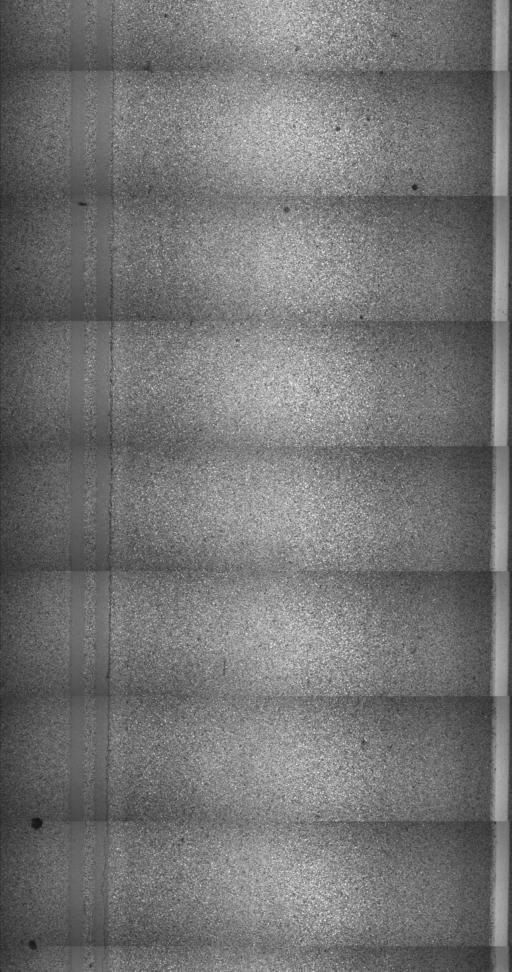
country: US
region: Vermont
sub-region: Rutland County
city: Poultney
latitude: 43.4348
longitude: -73.1116
